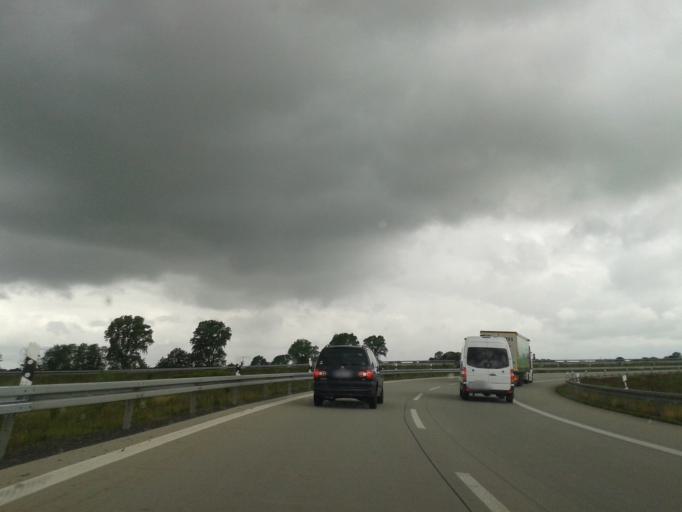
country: DE
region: Saxony
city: Borsdorf
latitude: 51.3117
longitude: 12.5480
